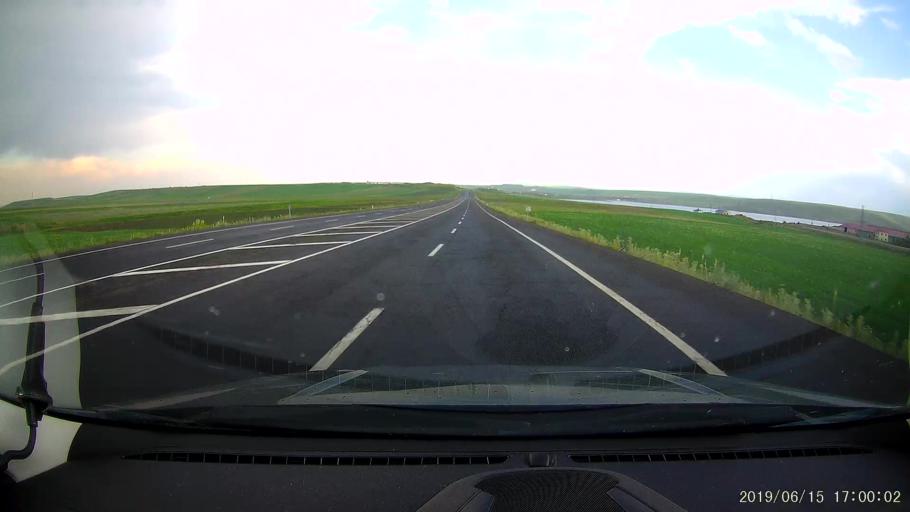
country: TR
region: Kars
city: Susuz
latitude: 40.7439
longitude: 43.1564
